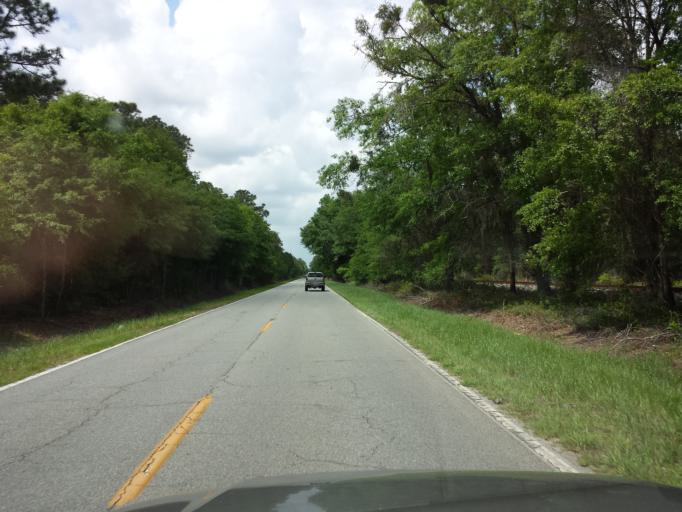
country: US
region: Georgia
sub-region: Echols County
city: Statenville
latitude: 30.6596
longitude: -83.1542
